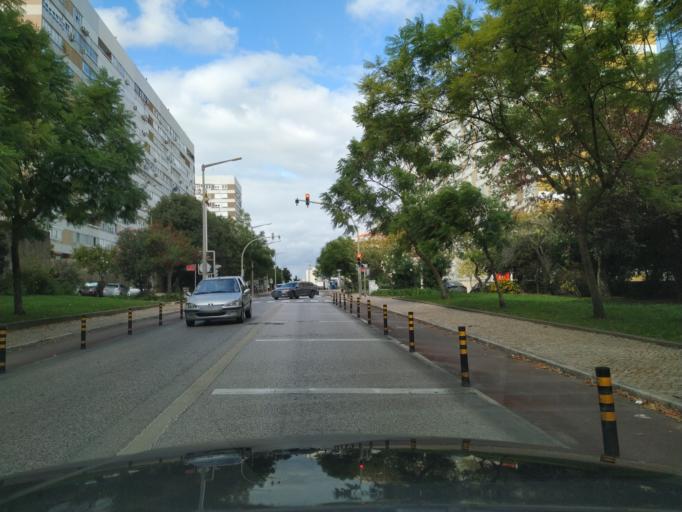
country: PT
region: Lisbon
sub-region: Loures
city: Sacavem
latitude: 38.7846
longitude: -9.1113
